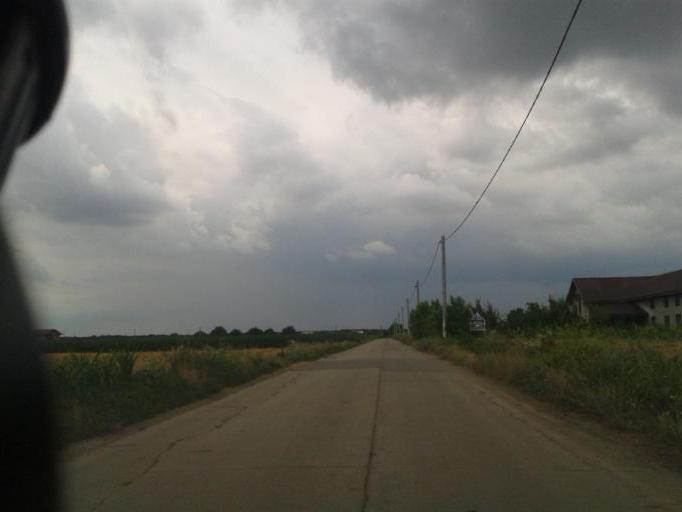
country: RO
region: Calarasi
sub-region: Comuna Fundulea
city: Fundulea
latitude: 44.4939
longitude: 26.5033
